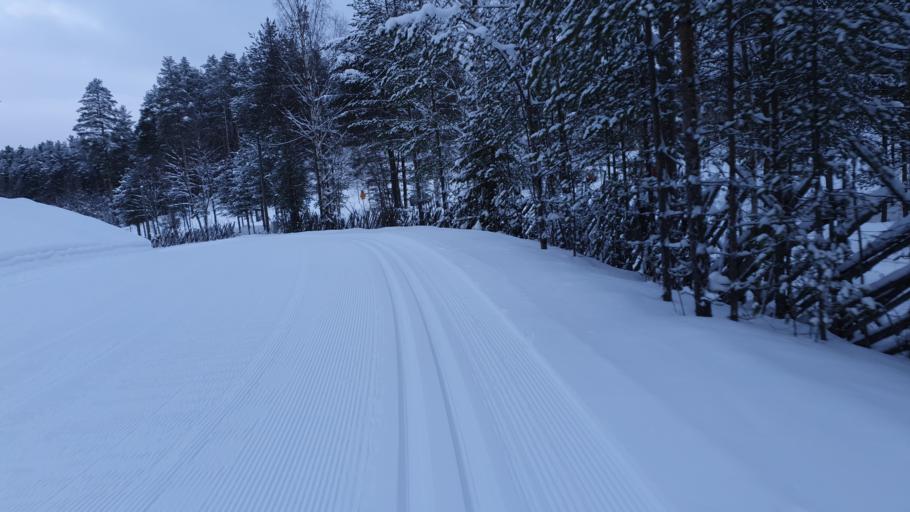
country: FI
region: Kainuu
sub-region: Kehys-Kainuu
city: Kuhmo
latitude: 64.1178
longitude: 29.5868
